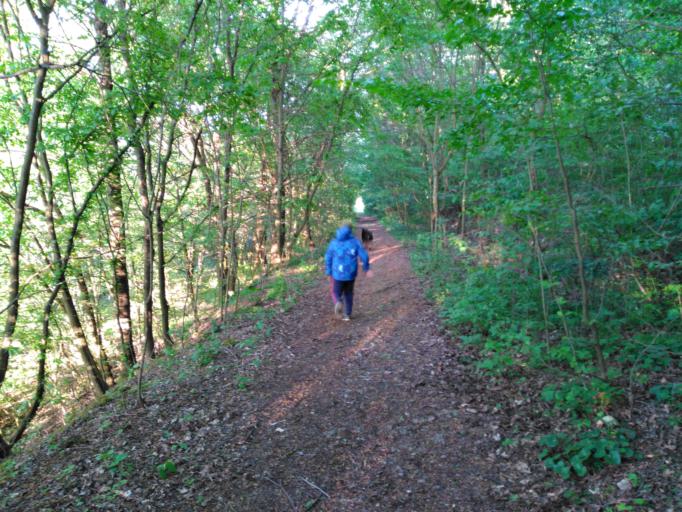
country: CZ
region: Central Bohemia
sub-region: Okres Beroun
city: Beroun
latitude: 49.9182
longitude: 14.0689
